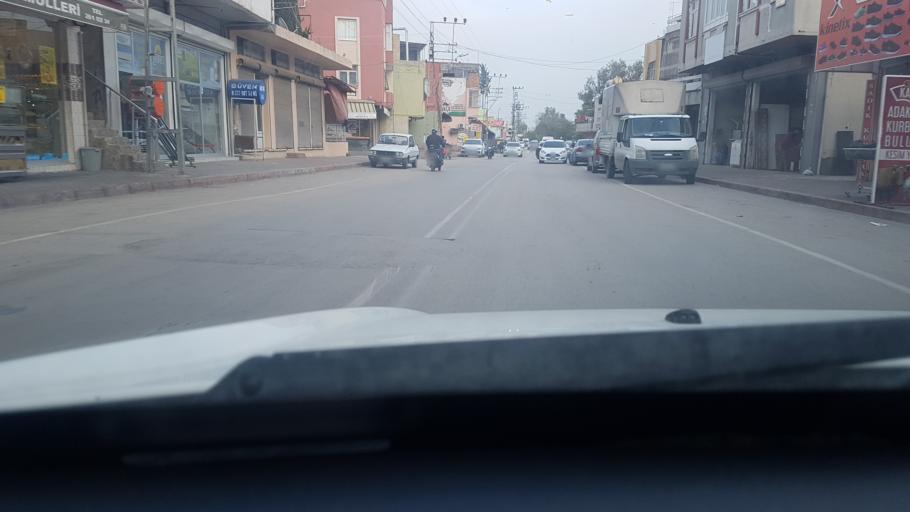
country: TR
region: Adana
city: Seyhan
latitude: 37.0139
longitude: 35.2784
